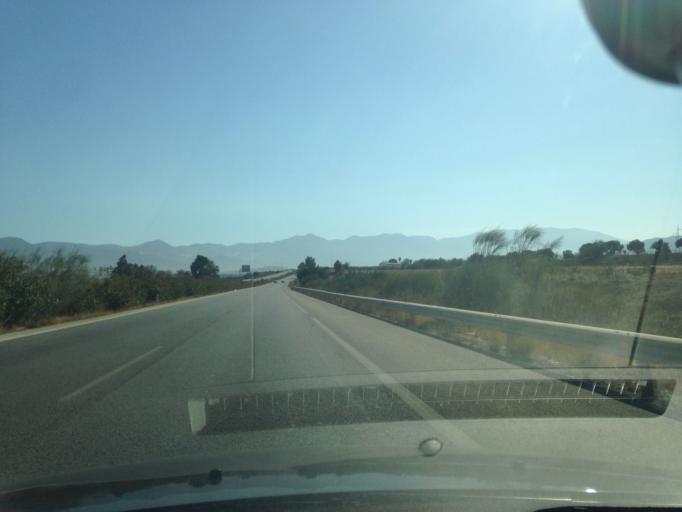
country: ES
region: Andalusia
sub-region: Provincia de Malaga
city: Estacion de Cartama
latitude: 36.7287
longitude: -4.5515
